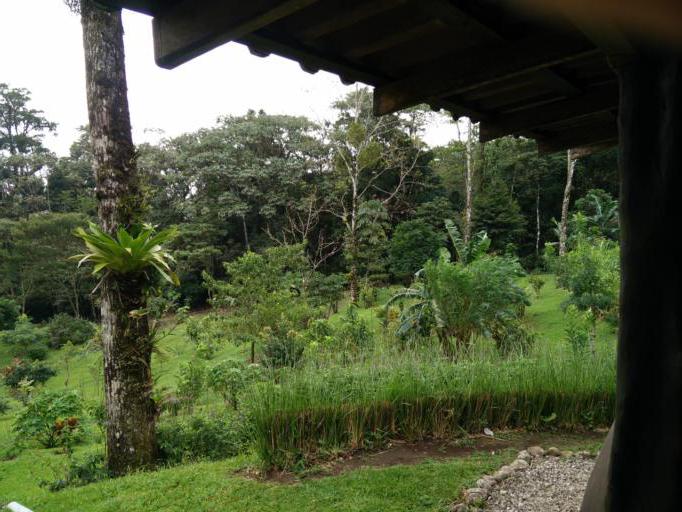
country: CR
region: Alajuela
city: Bijagua
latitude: 10.7152
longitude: -85.0388
